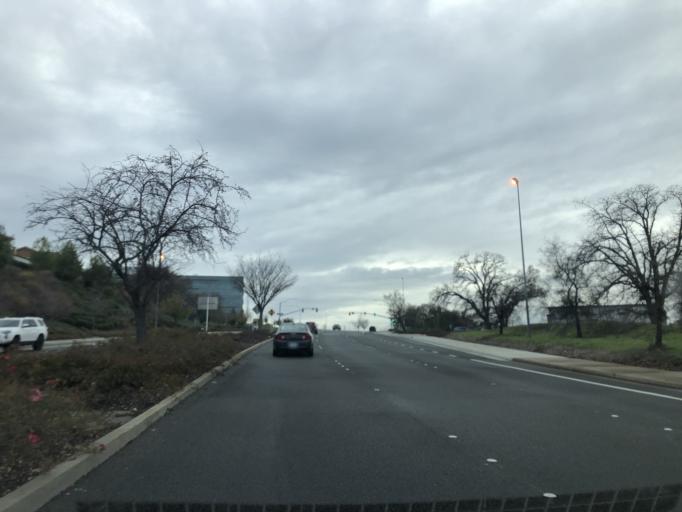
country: US
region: California
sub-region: Placer County
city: Rocklin
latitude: 38.7601
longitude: -121.2518
